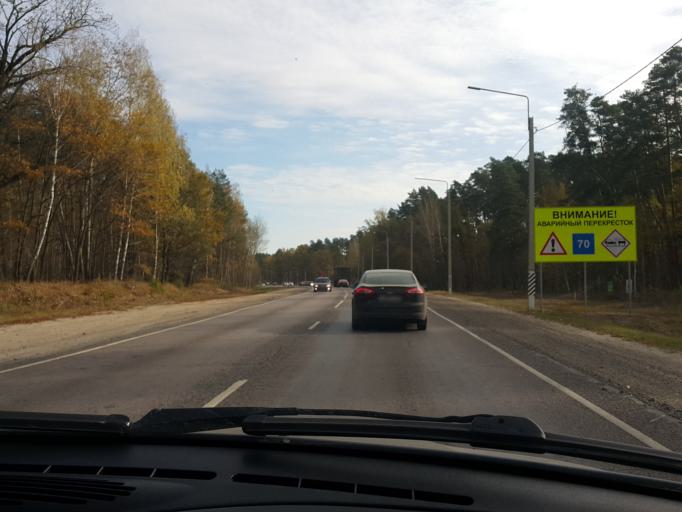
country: RU
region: Tambov
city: Donskoye
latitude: 52.7073
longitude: 41.5402
